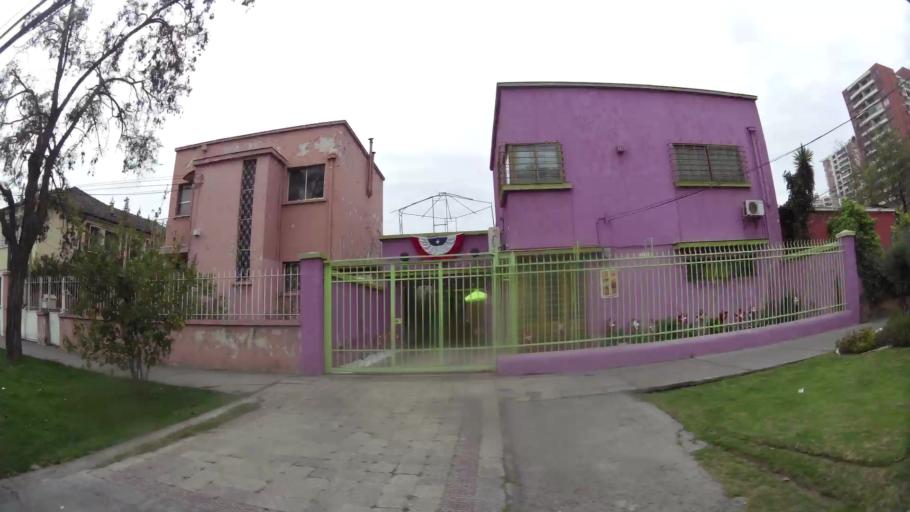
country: CL
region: Santiago Metropolitan
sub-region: Provincia de Santiago
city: Santiago
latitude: -33.4512
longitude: -70.6180
